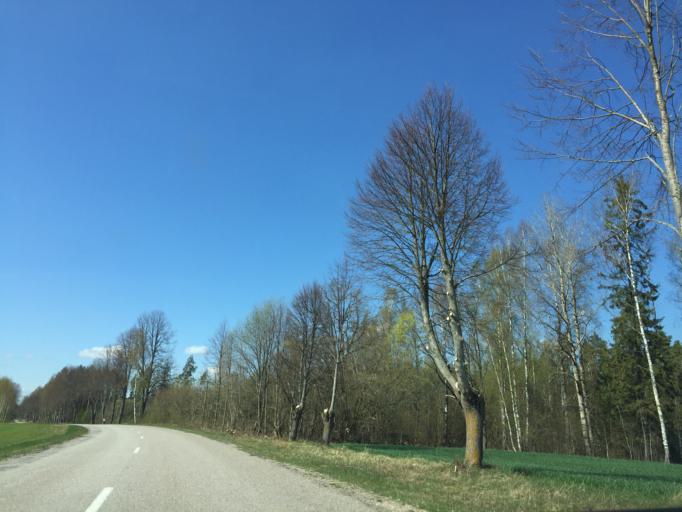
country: LV
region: Strenci
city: Seda
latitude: 57.5711
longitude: 25.8022
